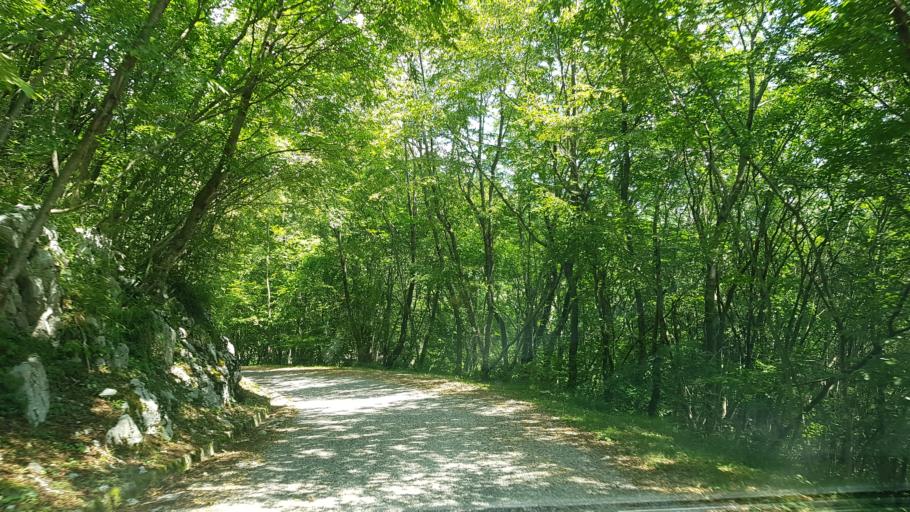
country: IT
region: Friuli Venezia Giulia
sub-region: Provincia di Udine
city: Nimis
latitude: 46.2363
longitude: 13.2556
